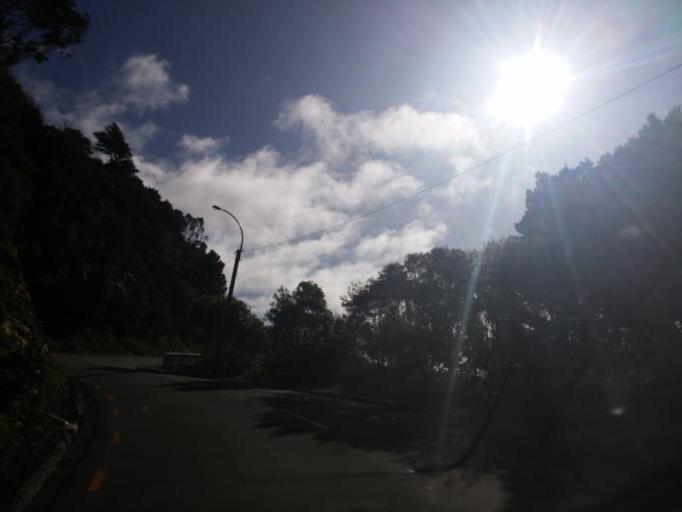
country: NZ
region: Wellington
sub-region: Wellington City
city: Kelburn
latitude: -41.2855
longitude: 174.7533
